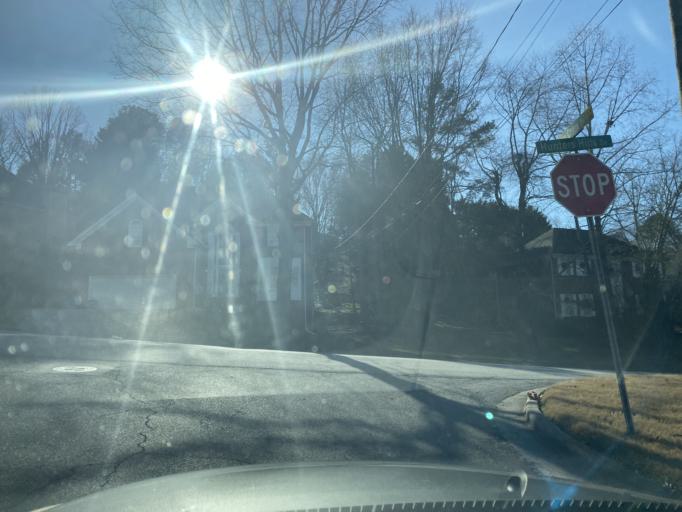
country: US
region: Georgia
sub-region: DeKalb County
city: Pine Mountain
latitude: 33.6843
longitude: -84.1594
